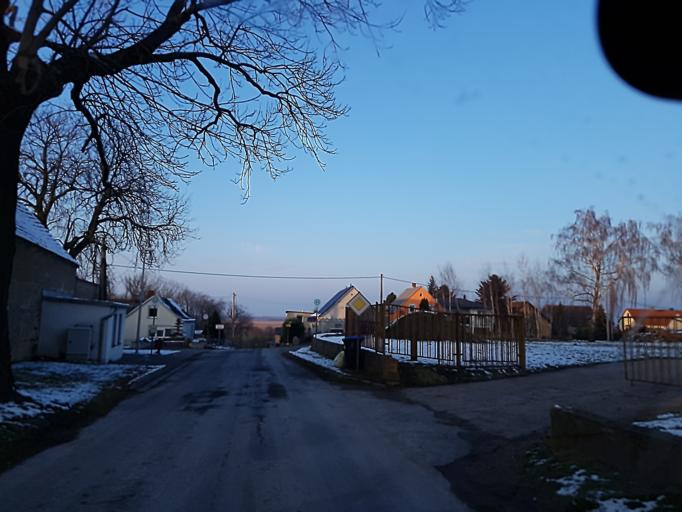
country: DE
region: Saxony
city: Strehla
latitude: 51.3704
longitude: 13.2238
